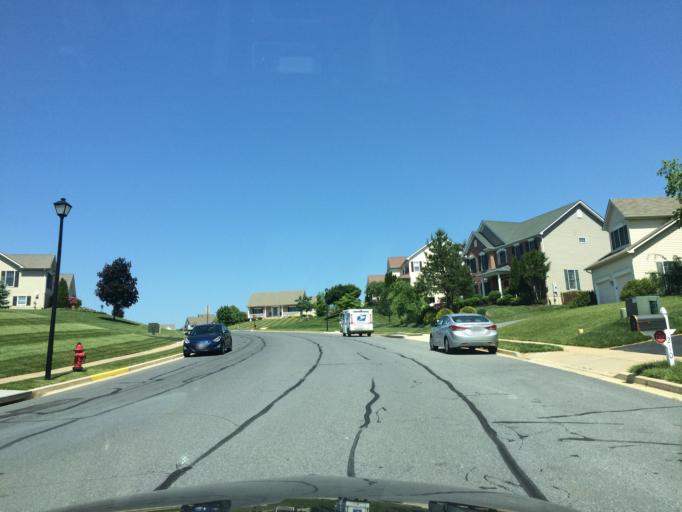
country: US
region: Maryland
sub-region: Frederick County
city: Middletown
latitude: 39.4456
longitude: -77.5156
